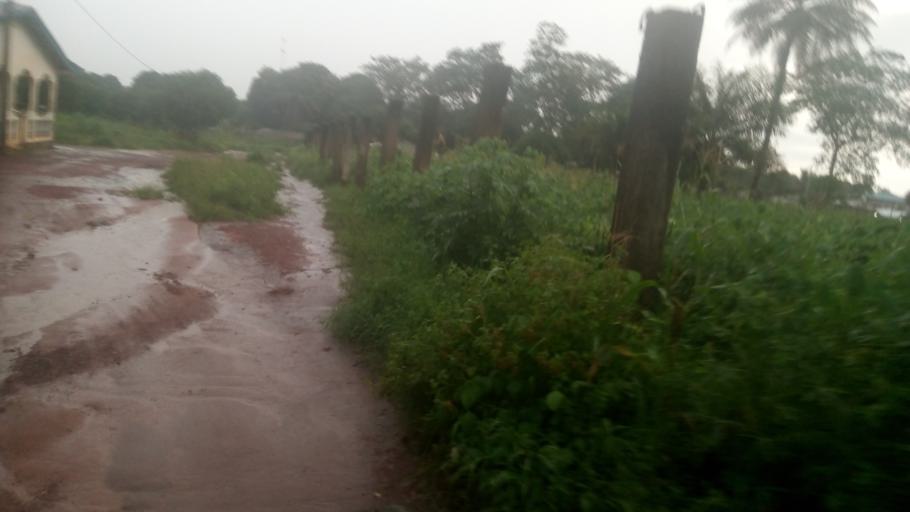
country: SL
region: Northern Province
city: Lunsar
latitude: 8.6927
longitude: -12.5326
